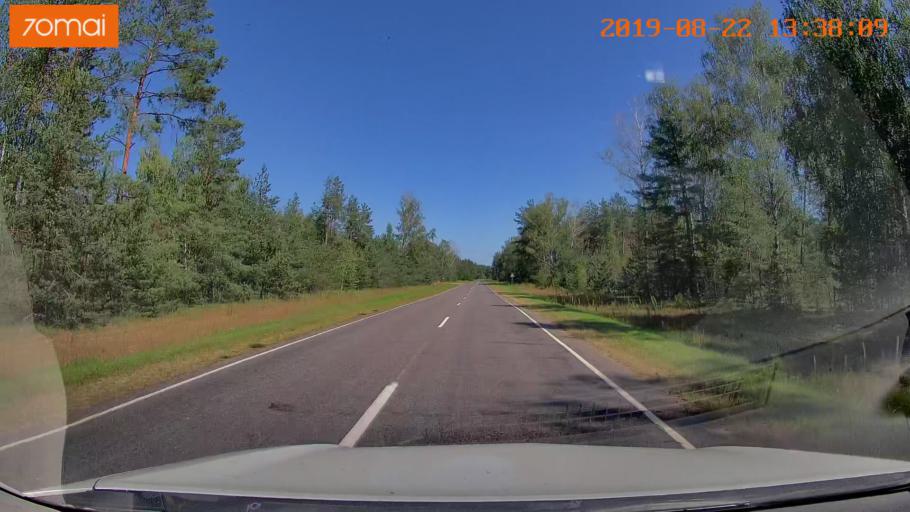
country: BY
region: Minsk
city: Staryya Darohi
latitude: 53.2214
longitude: 28.3157
